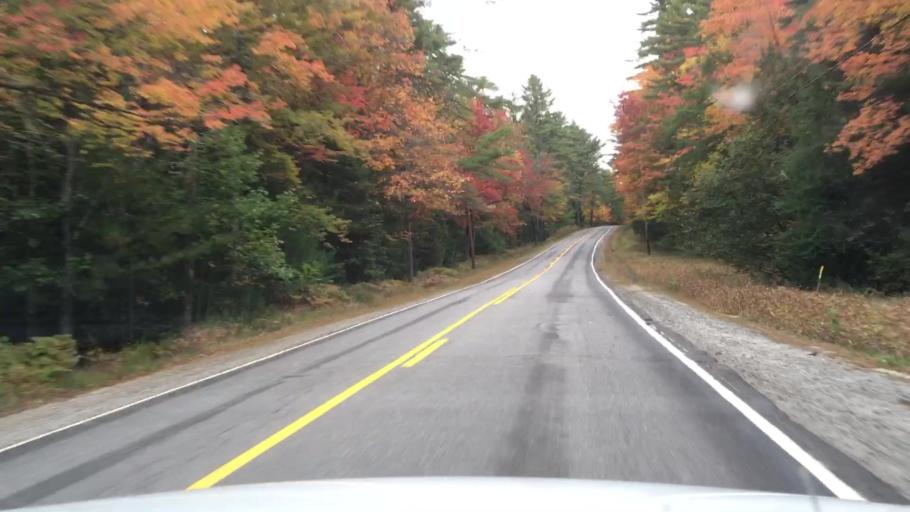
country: US
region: Maine
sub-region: Oxford County
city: Bethel
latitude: 44.3854
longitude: -70.7983
